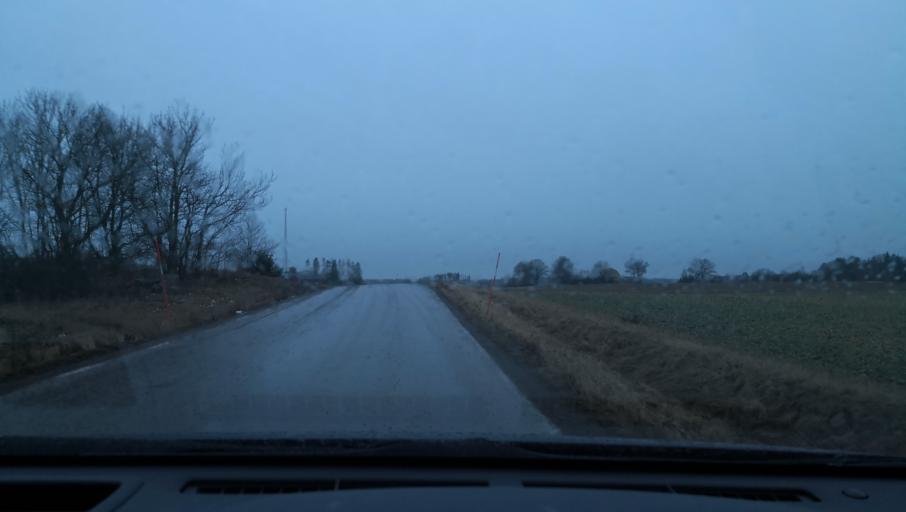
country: SE
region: Soedermanland
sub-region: Eskilstuna Kommun
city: Arla
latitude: 59.4426
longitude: 16.7188
